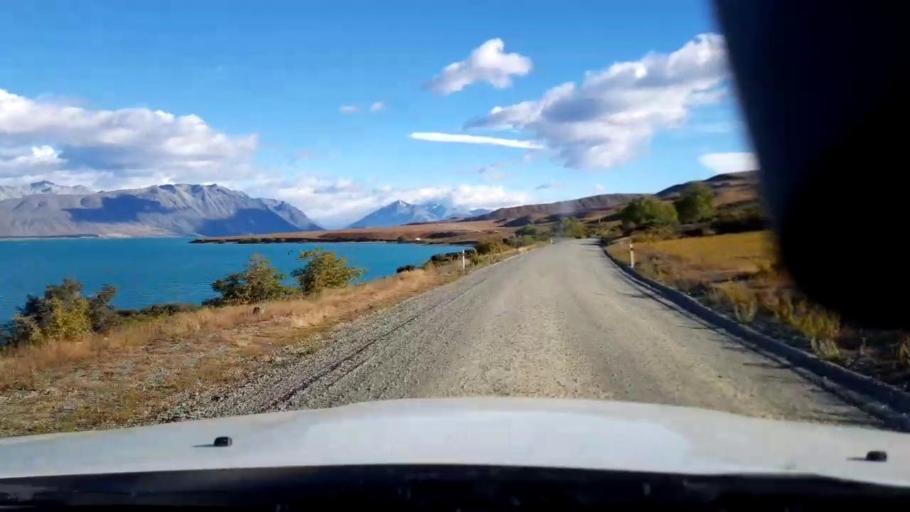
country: NZ
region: Canterbury
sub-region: Timaru District
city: Pleasant Point
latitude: -43.9324
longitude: 170.5590
